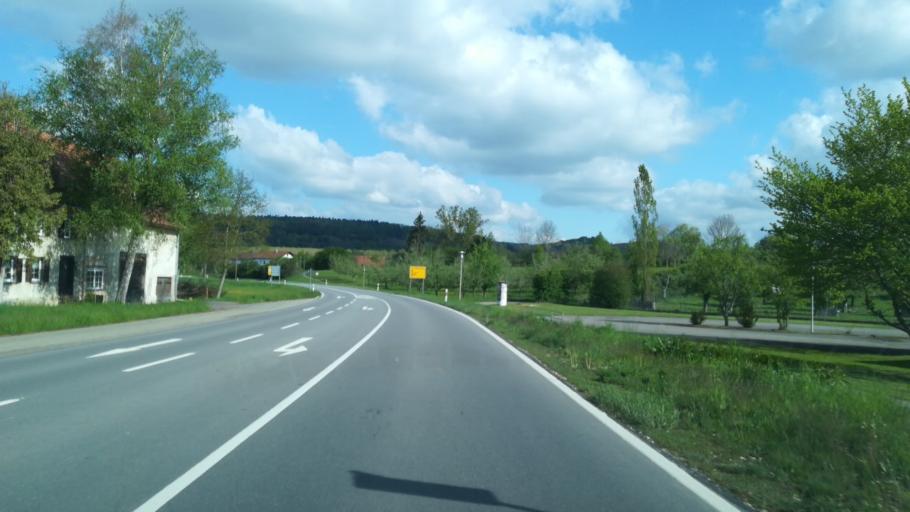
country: CH
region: Schaffhausen
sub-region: Bezirk Reiat
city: Thayngen
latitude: 47.7934
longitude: 8.7207
